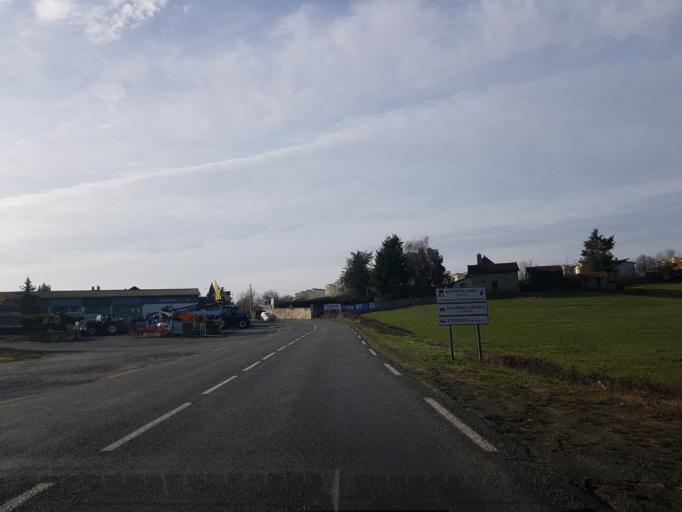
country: FR
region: Bourgogne
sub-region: Departement de Saone-et-Loire
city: Bourbon-Lancy
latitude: 46.6237
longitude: 3.7809
